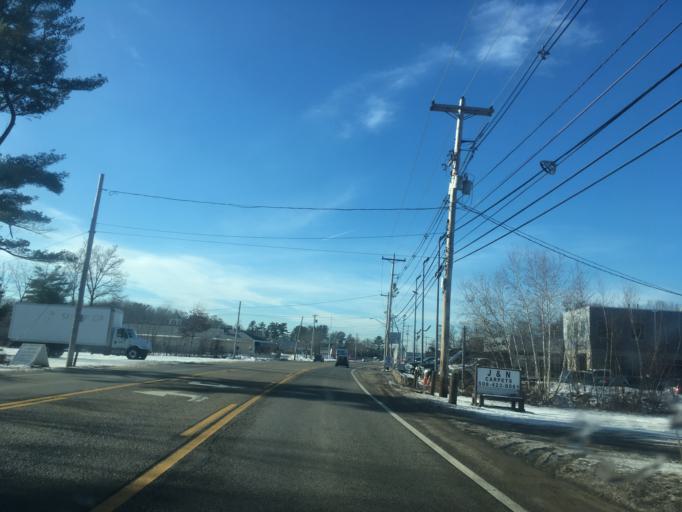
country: US
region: Massachusetts
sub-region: Essex County
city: Salisbury
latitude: 42.8439
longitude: -70.8881
